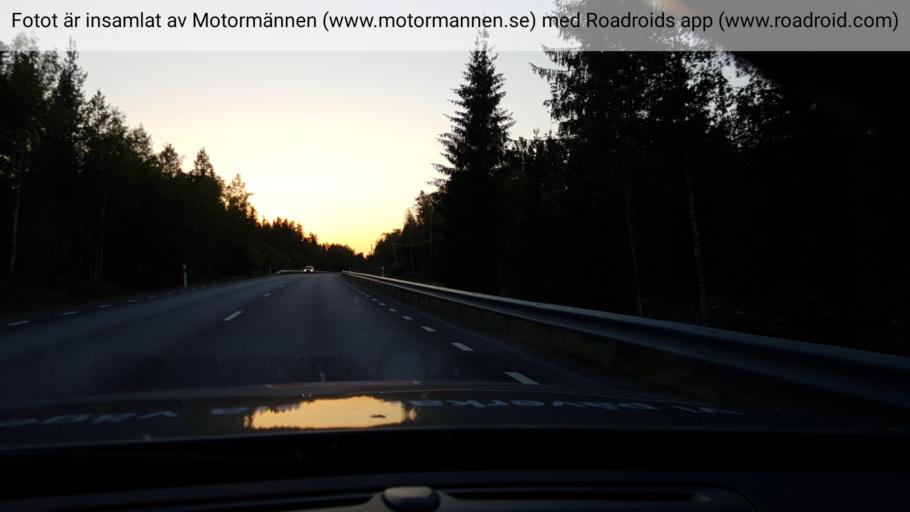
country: SE
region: Uppsala
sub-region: Osthammars Kommun
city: Bjorklinge
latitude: 59.9809
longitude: 17.3378
